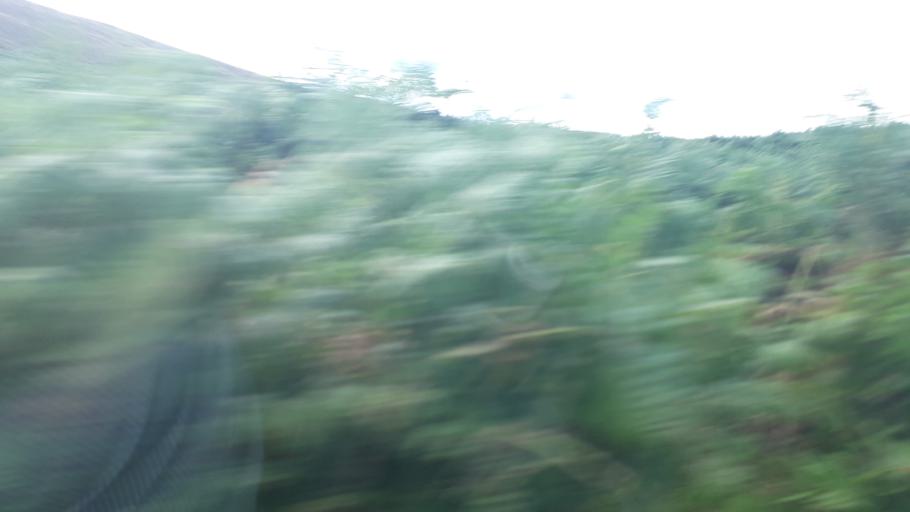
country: GB
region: Northern Ireland
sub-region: Down District
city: Warrenpoint
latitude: 54.0583
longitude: -6.2738
